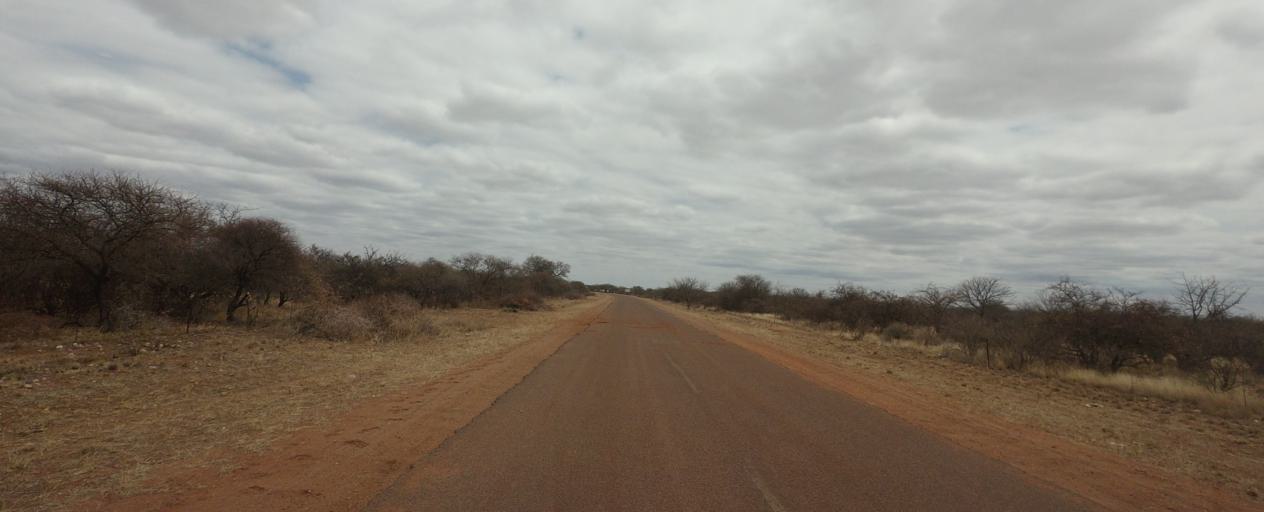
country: BW
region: Central
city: Makobeng
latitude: -22.8442
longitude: 28.2064
